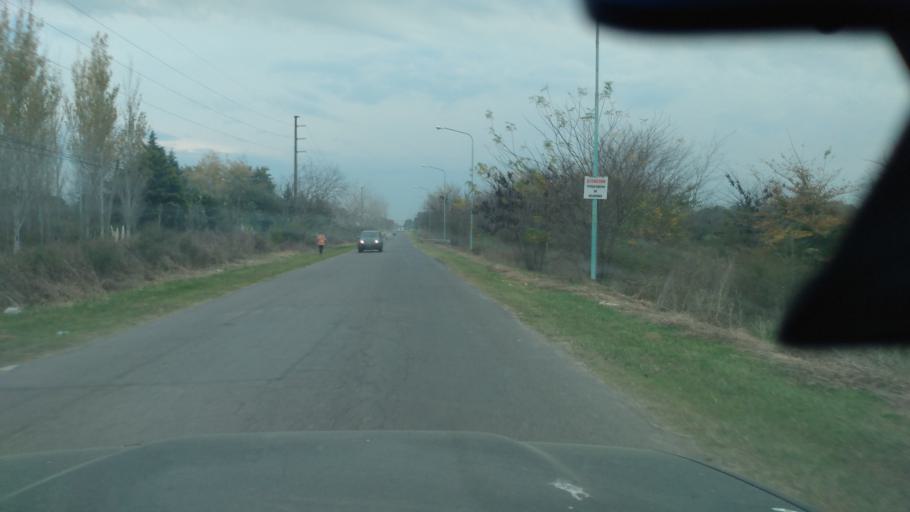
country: AR
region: Buenos Aires
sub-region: Partido de Lujan
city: Lujan
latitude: -34.5672
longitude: -59.1472
